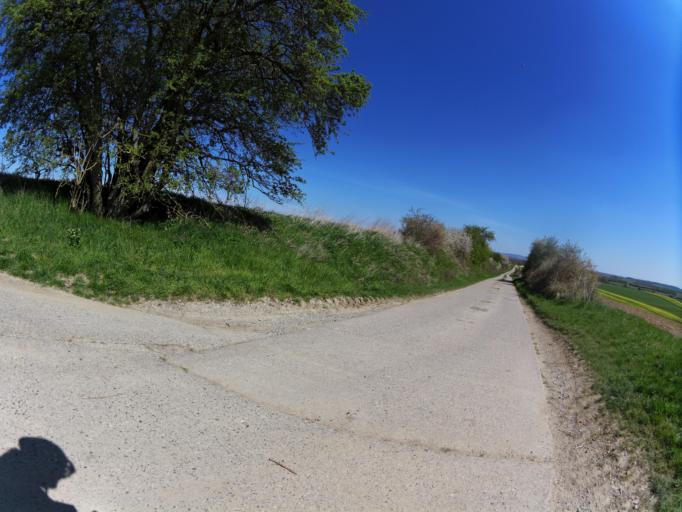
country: DE
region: Bavaria
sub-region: Regierungsbezirk Unterfranken
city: Winterhausen
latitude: 49.6817
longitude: 9.9898
